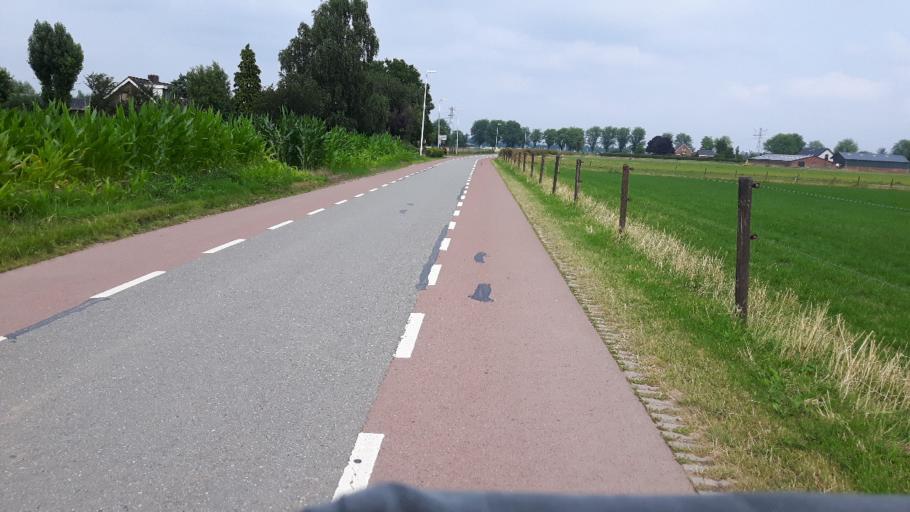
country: NL
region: Utrecht
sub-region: Gemeente Bunnik
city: Bunnik
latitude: 52.0467
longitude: 5.1897
